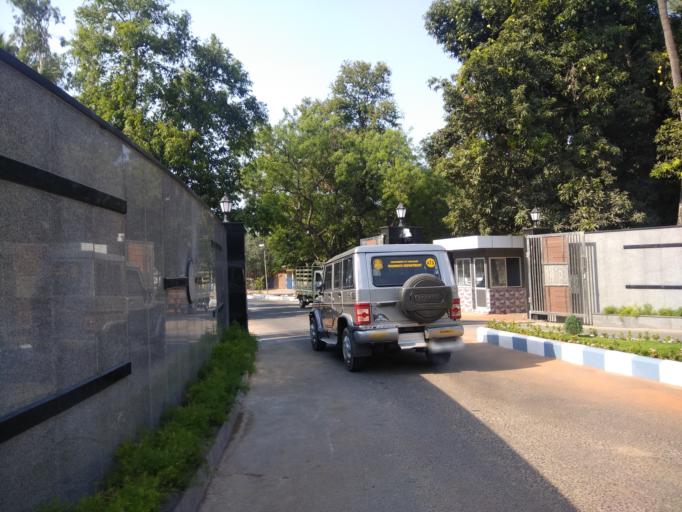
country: IN
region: Tamil Nadu
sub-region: Chennai
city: Gandhi Nagar
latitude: 13.0090
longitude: 80.2301
